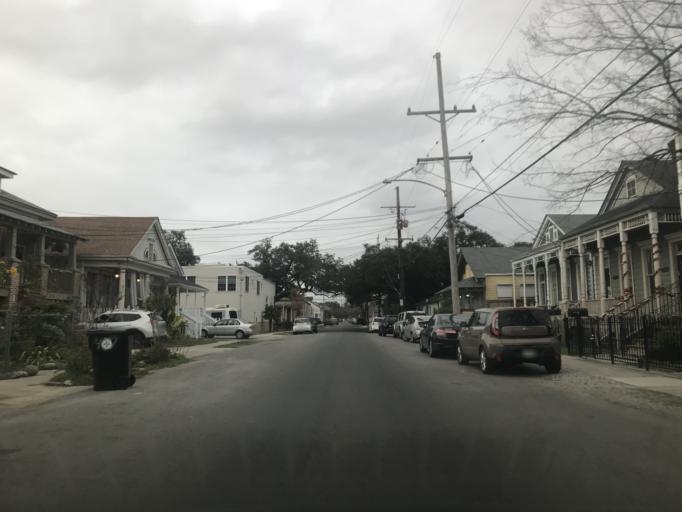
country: US
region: Louisiana
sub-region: Orleans Parish
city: New Orleans
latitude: 29.9644
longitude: -90.0935
